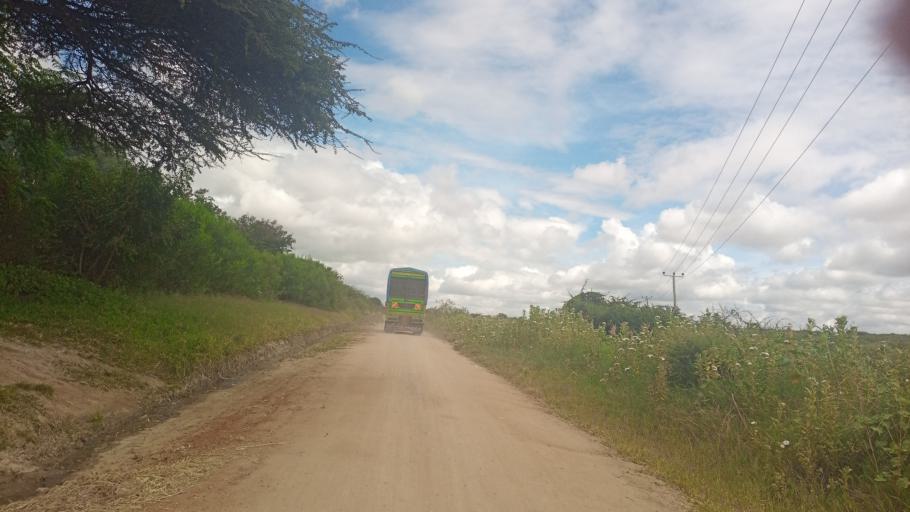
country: TZ
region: Dodoma
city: Dodoma
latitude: -6.1889
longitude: 35.7182
